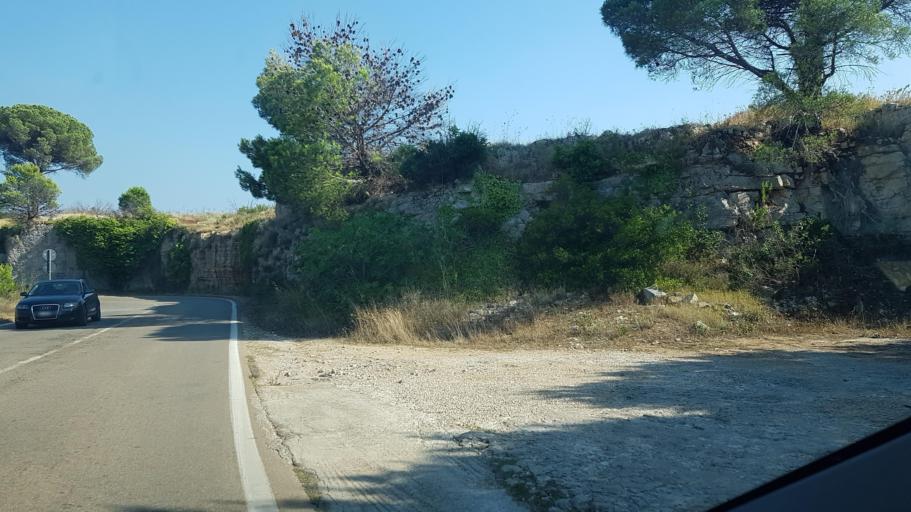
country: IT
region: Apulia
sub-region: Provincia di Lecce
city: Presicce
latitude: 39.8932
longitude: 18.2544
